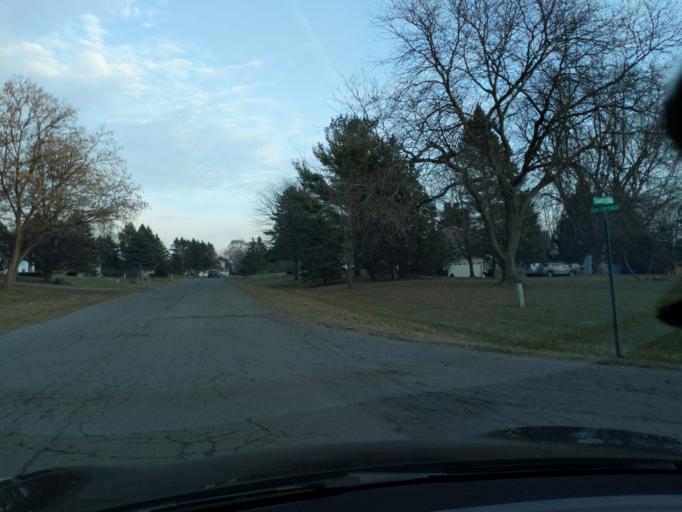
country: US
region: Michigan
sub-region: Livingston County
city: Brighton
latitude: 42.6429
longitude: -83.7196
